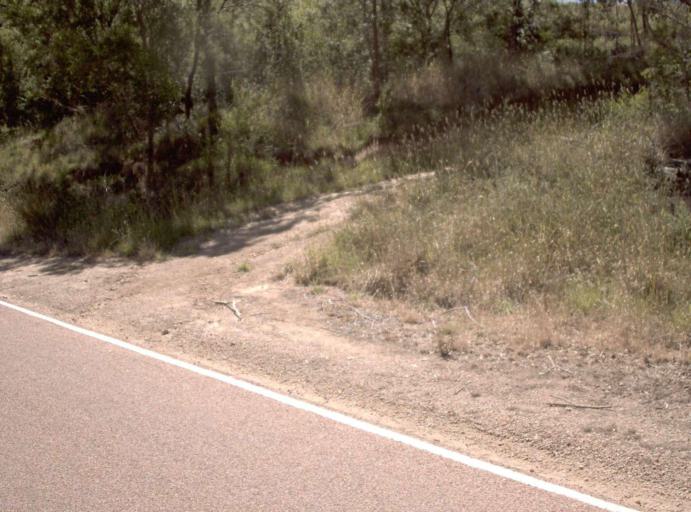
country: AU
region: Victoria
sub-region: East Gippsland
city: Lakes Entrance
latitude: -37.4770
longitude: 148.1821
